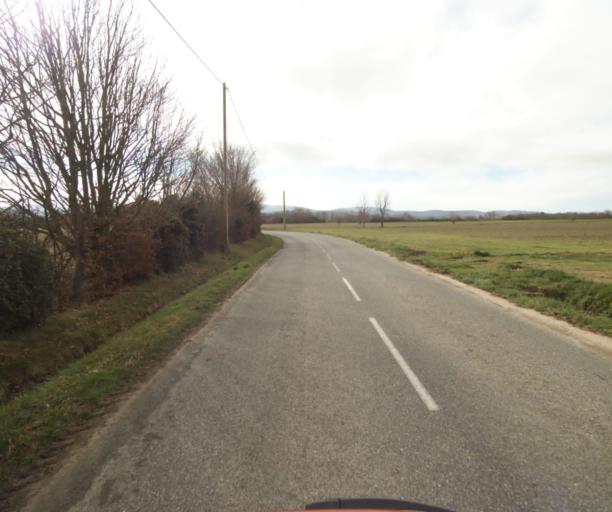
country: FR
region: Midi-Pyrenees
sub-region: Departement de l'Ariege
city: Pamiers
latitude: 43.1152
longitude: 1.5455
